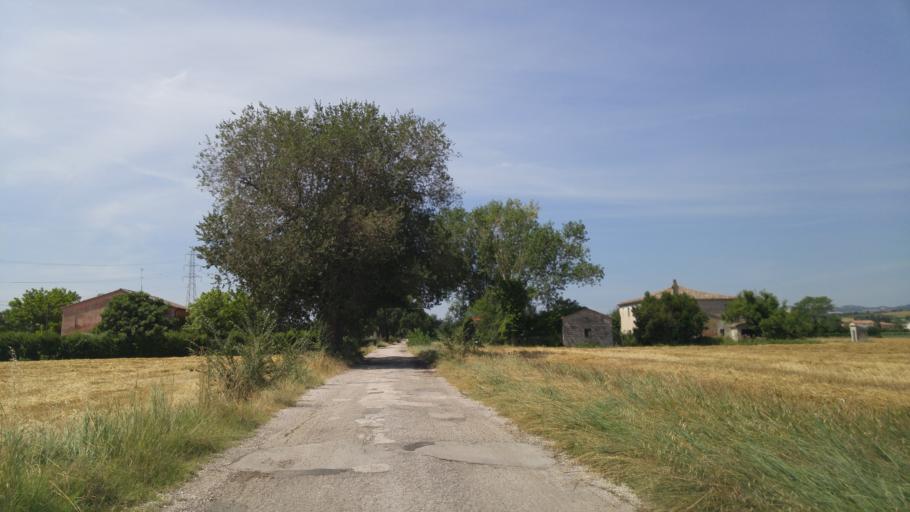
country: IT
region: The Marches
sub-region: Provincia di Pesaro e Urbino
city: Cuccurano
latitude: 43.7941
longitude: 12.9683
